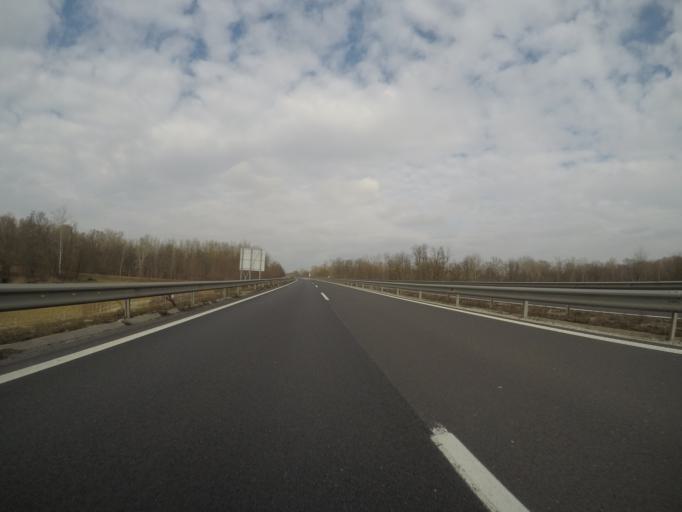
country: SI
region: Murska Sobota
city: Bakovci
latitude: 46.6014
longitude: 16.1245
